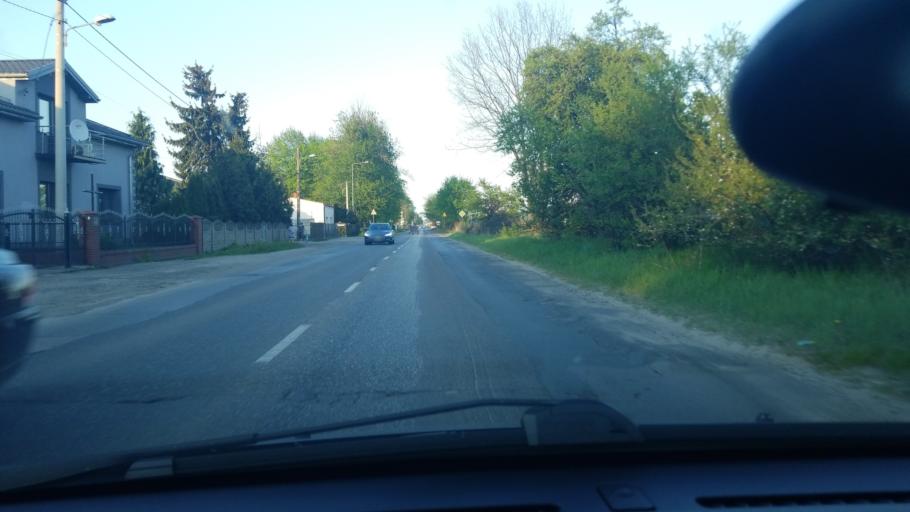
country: PL
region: Silesian Voivodeship
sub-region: Powiat klobucki
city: Kalej
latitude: 50.7937
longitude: 19.0373
